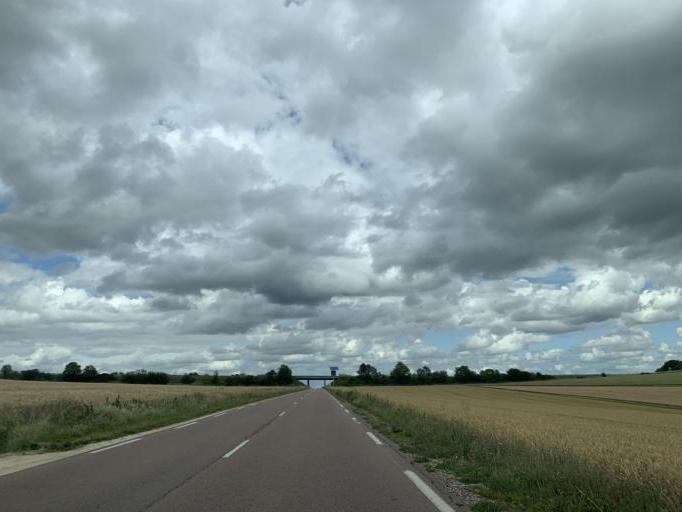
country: FR
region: Bourgogne
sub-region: Departement de l'Yonne
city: Vermenton
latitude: 47.7371
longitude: 3.7278
